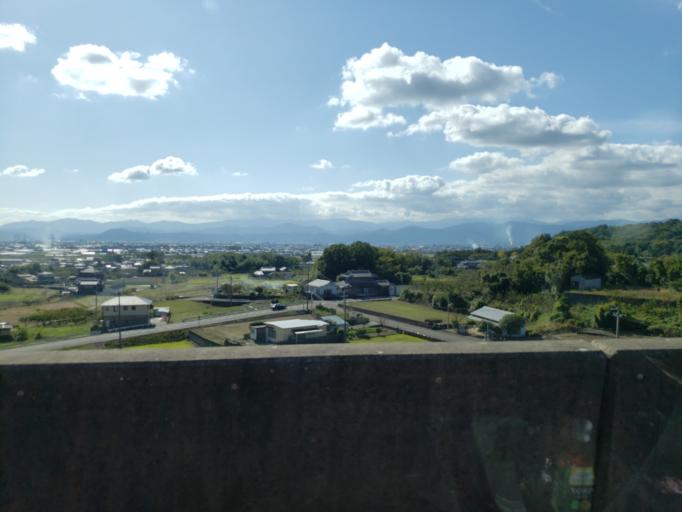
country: JP
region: Tokushima
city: Ishii
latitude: 34.1431
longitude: 134.4343
